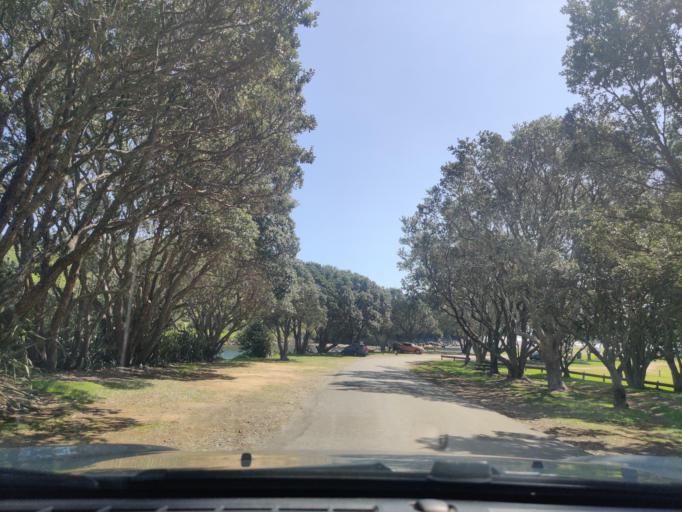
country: NZ
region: Taranaki
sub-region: New Plymouth District
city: New Plymouth
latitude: -39.1115
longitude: 173.9584
